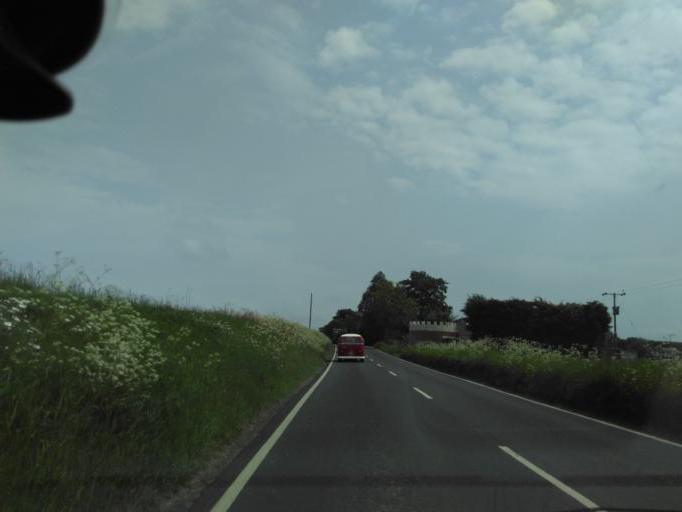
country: GB
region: England
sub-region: Kent
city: Canterbury
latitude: 51.2359
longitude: 1.0676
